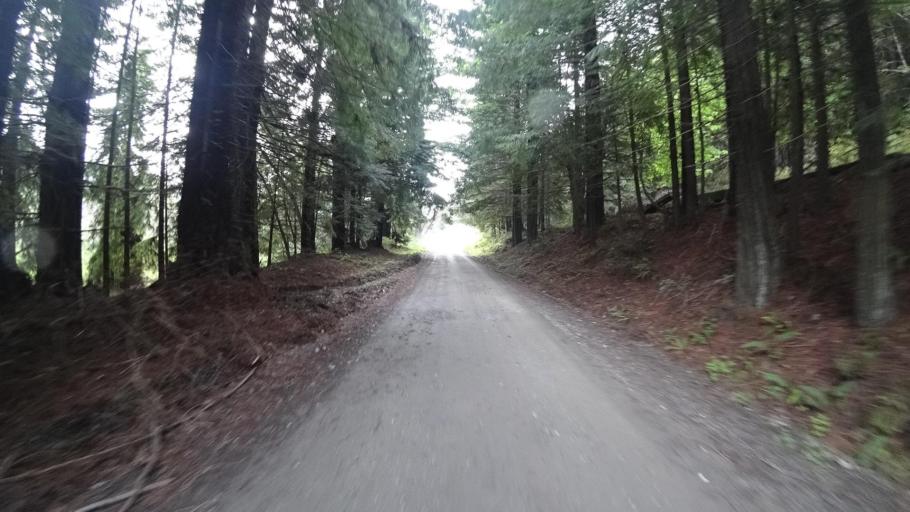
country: US
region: California
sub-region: Humboldt County
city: Redway
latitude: 40.3253
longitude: -123.8386
